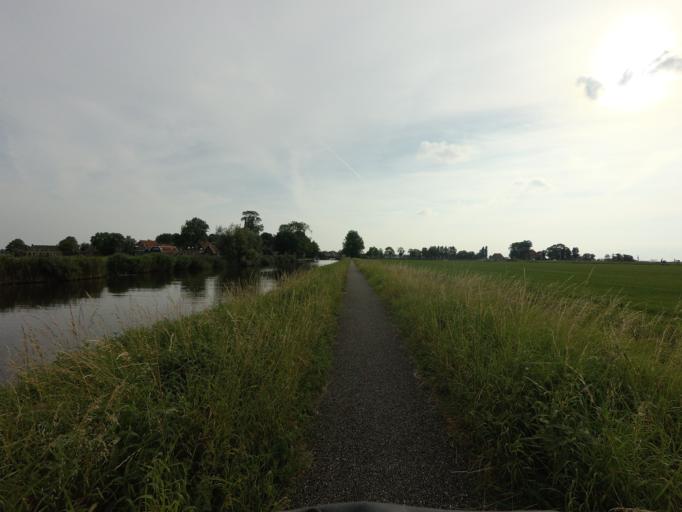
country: NL
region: Friesland
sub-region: Sudwest Fryslan
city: Bolsward
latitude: 53.0448
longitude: 5.5021
